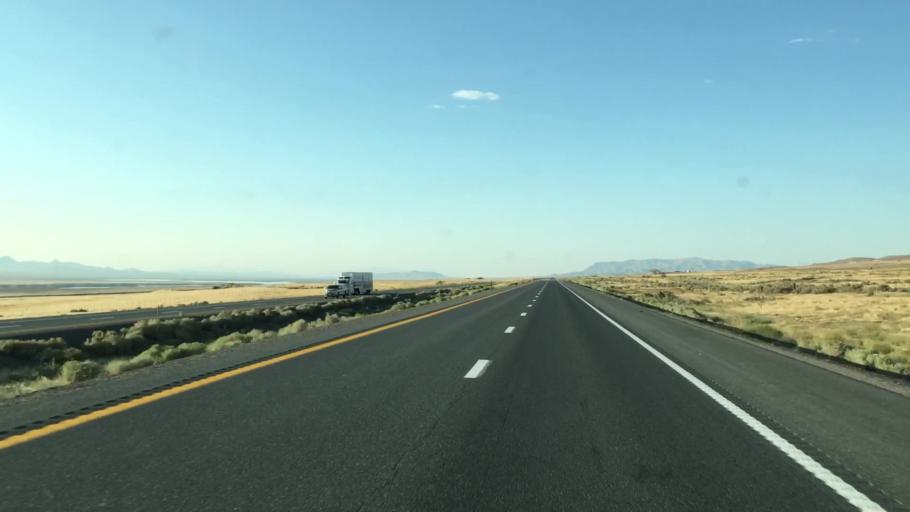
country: US
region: Nevada
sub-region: Pershing County
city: Lovelock
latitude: 40.4964
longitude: -118.2836
